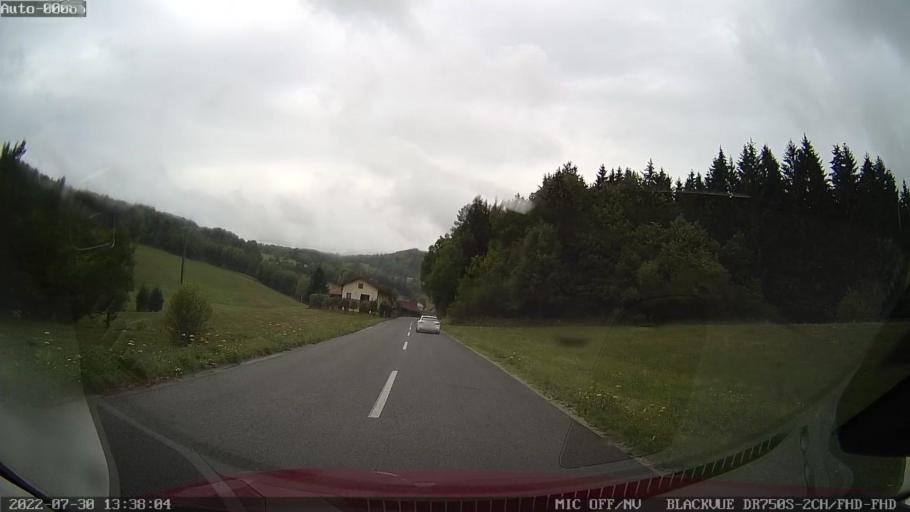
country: SI
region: Zuzemberk
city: Zuzemberk
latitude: 45.8818
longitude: 14.9128
